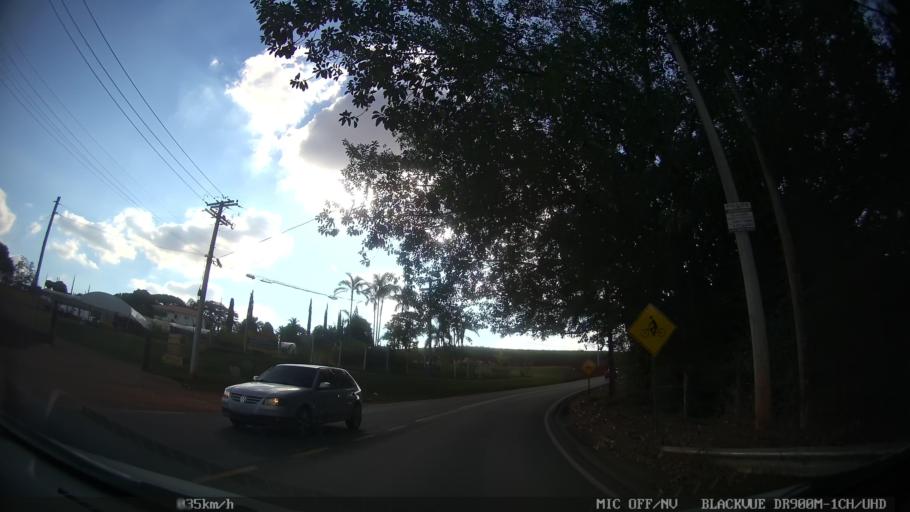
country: BR
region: Sao Paulo
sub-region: Nova Odessa
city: Nova Odessa
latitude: -22.7934
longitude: -47.3368
